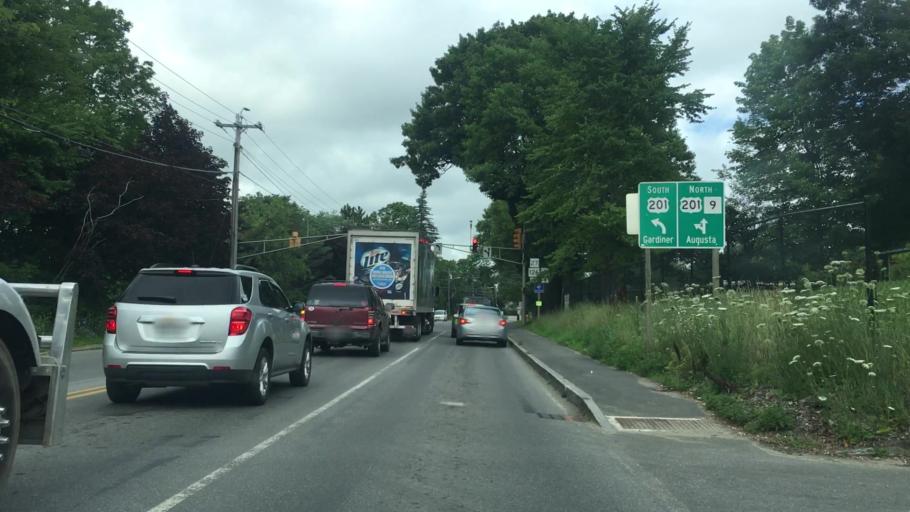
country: US
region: Maine
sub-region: Kennebec County
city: Randolph
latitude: 44.2325
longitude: -69.7676
